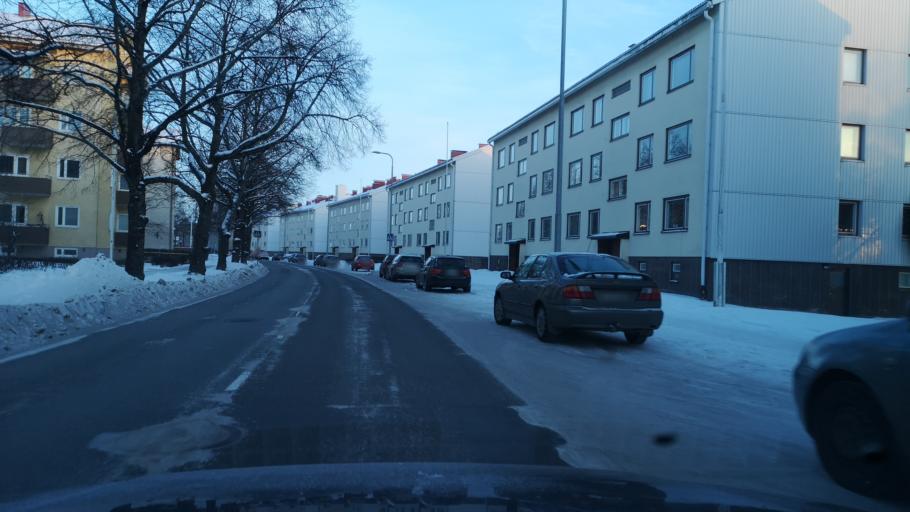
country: FI
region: Satakunta
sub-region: Pori
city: Pori
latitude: 61.4773
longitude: 21.7948
